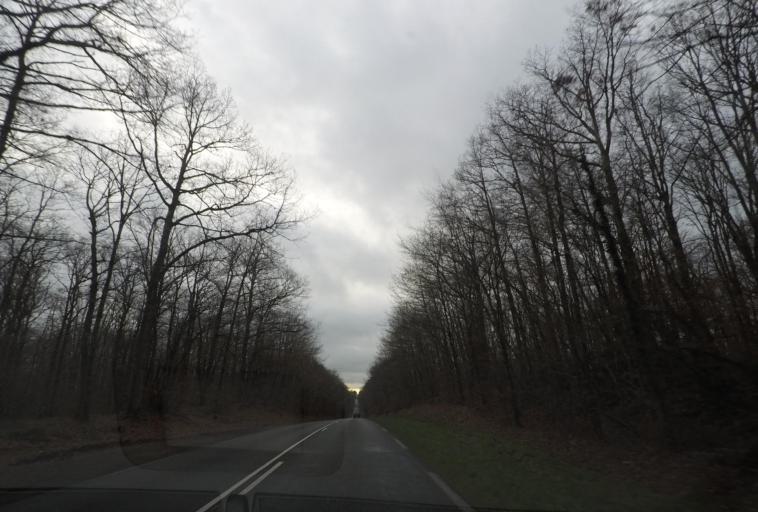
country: FR
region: Pays de la Loire
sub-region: Departement de la Sarthe
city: Vibraye
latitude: 48.0266
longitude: 0.7497
